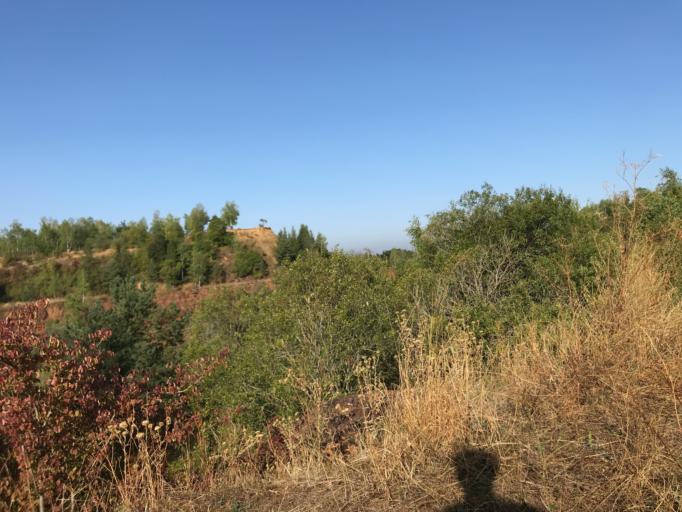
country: LU
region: Luxembourg
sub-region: Canton d'Esch-sur-Alzette
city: Niedercorn
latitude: 49.5419
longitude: 5.8824
